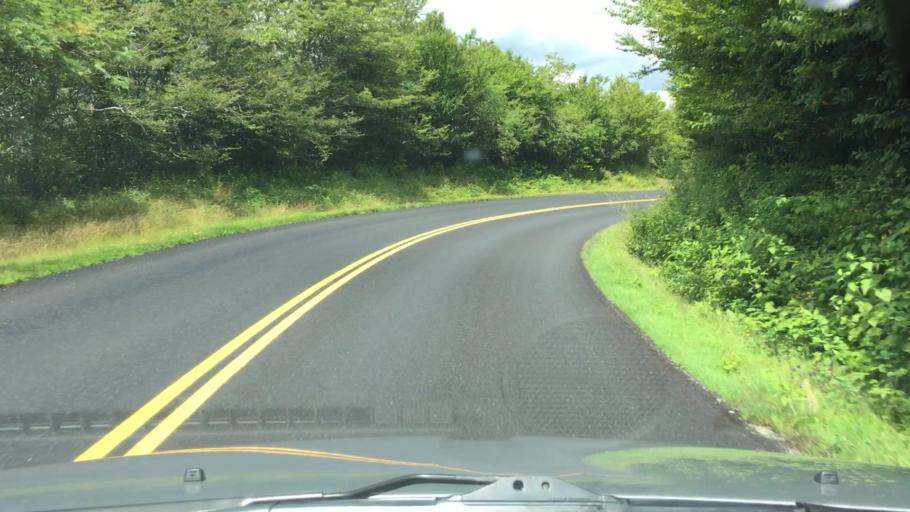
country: US
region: North Carolina
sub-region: Buncombe County
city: Black Mountain
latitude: 35.7179
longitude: -82.3602
